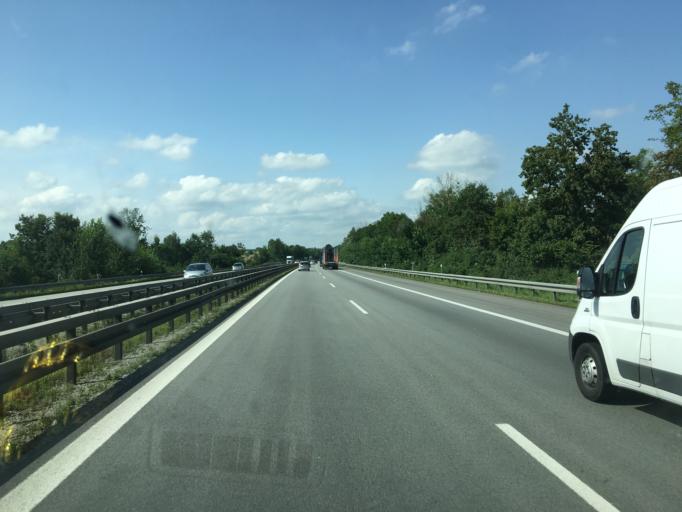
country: AT
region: Upper Austria
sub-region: Politischer Bezirk Scharding
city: Scharding
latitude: 48.4676
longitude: 13.3726
